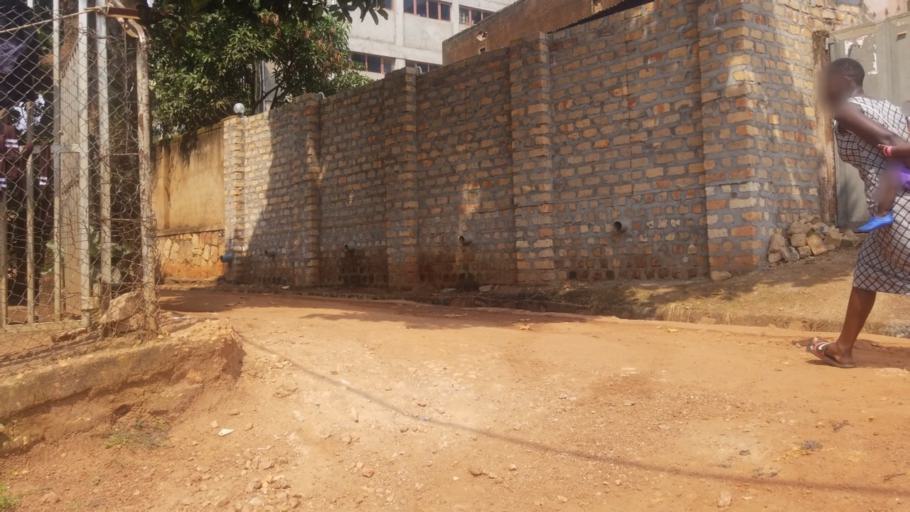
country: UG
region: Central Region
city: Kampala Central Division
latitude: 0.3408
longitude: 32.5555
